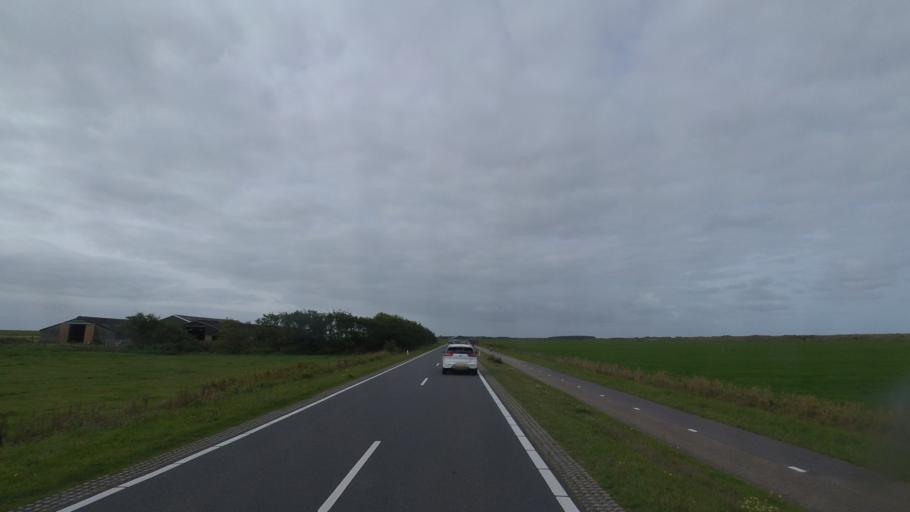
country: NL
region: Friesland
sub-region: Gemeente Ameland
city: Nes
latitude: 53.4458
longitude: 5.7468
